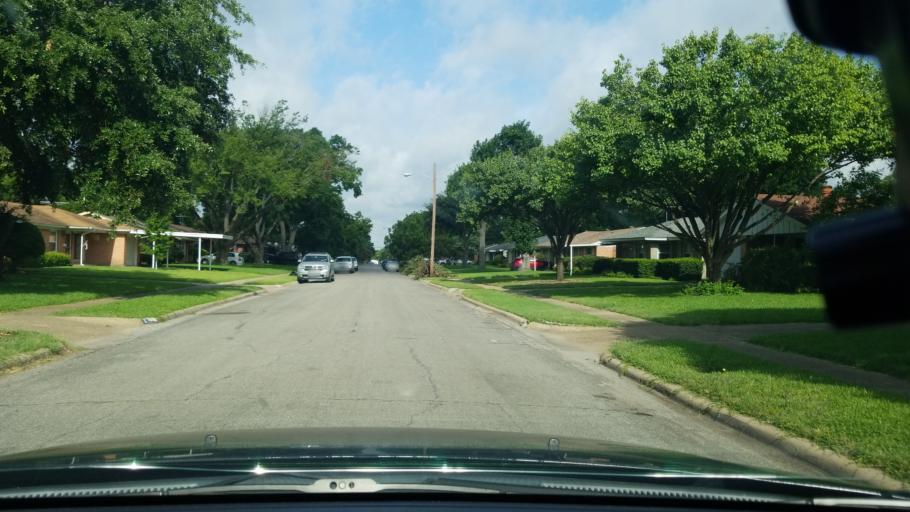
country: US
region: Texas
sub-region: Dallas County
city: Mesquite
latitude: 32.8152
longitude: -96.6706
